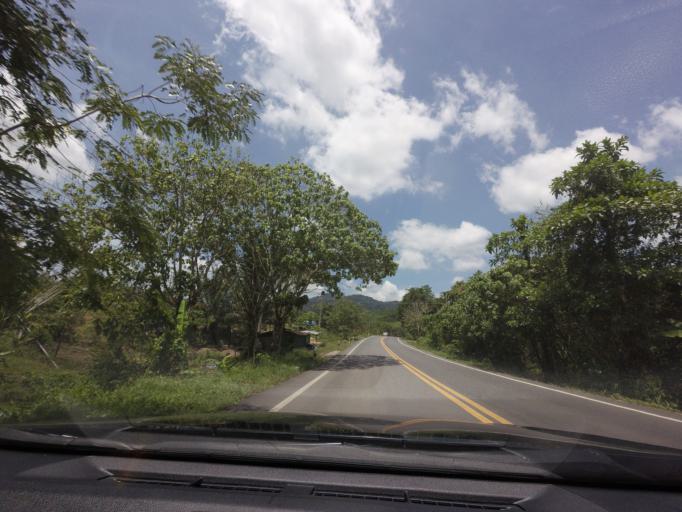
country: TH
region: Chumphon
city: Ban Nam Yuen
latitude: 9.9069
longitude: 98.9024
